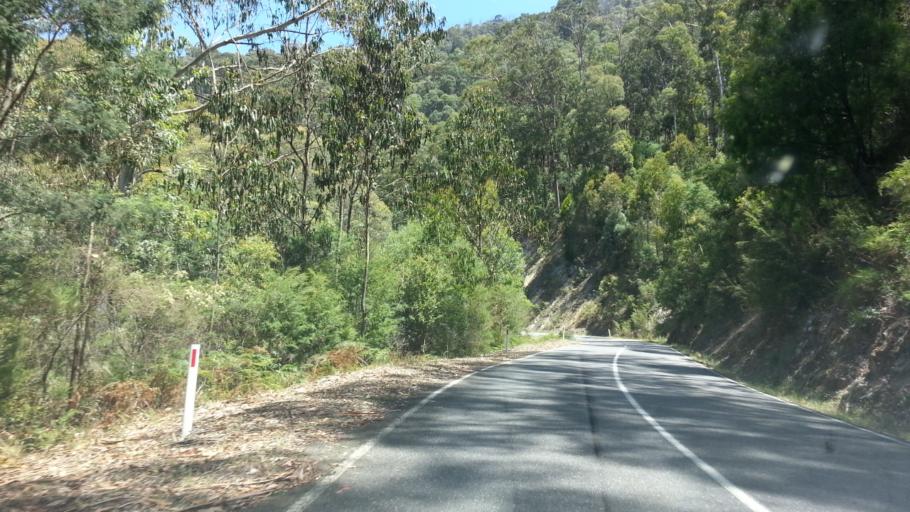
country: AU
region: Victoria
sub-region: Alpine
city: Mount Beauty
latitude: -36.7700
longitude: 147.2135
